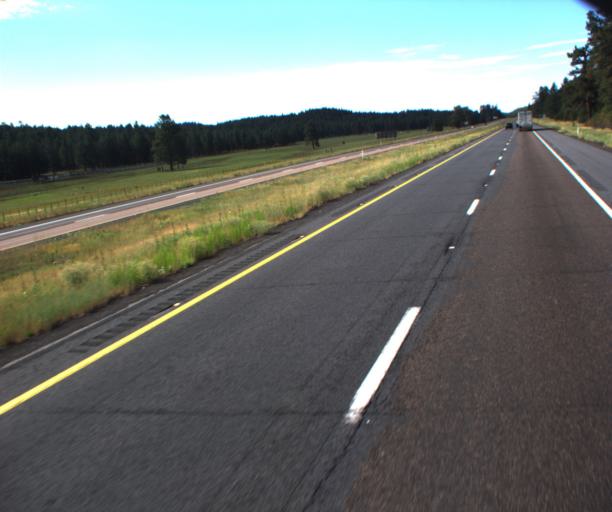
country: US
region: Arizona
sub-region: Coconino County
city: Mountainaire
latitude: 35.0108
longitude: -111.6854
